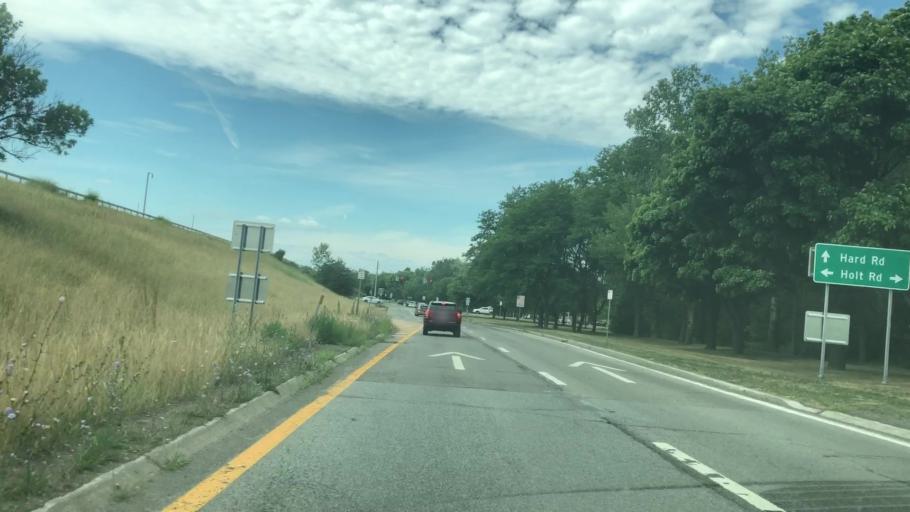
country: US
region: New York
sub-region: Monroe County
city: Webster
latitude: 43.2159
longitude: -77.4445
